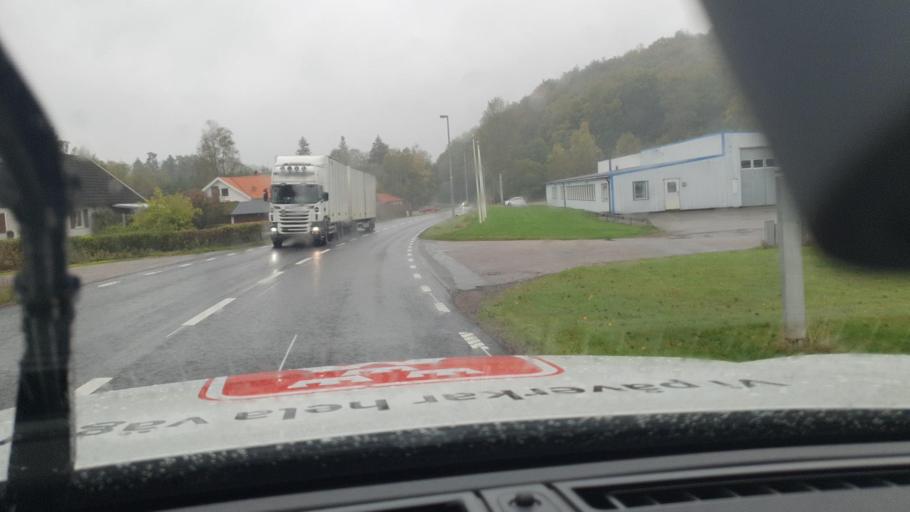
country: SE
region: Vaestra Goetaland
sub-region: Marks Kommun
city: Horred
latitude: 57.1633
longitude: 12.7456
